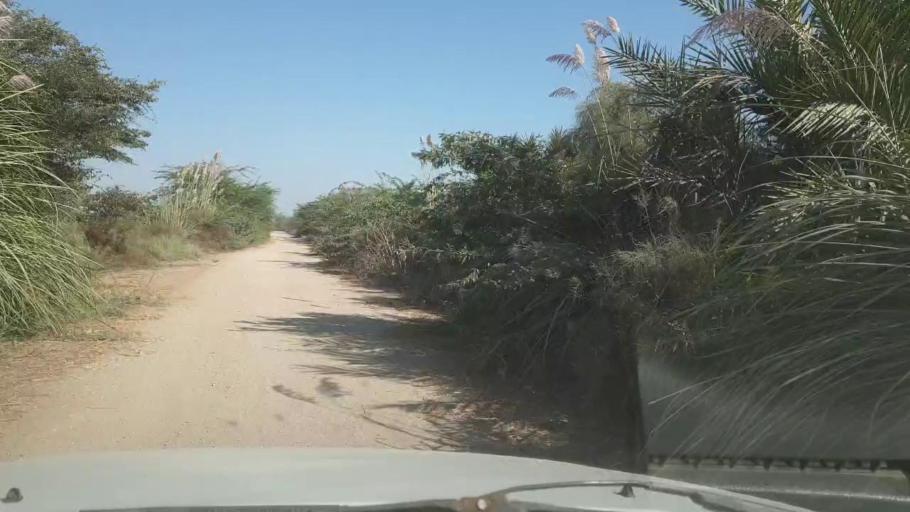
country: PK
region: Sindh
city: Mirpur Sakro
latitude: 24.4640
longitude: 67.7629
